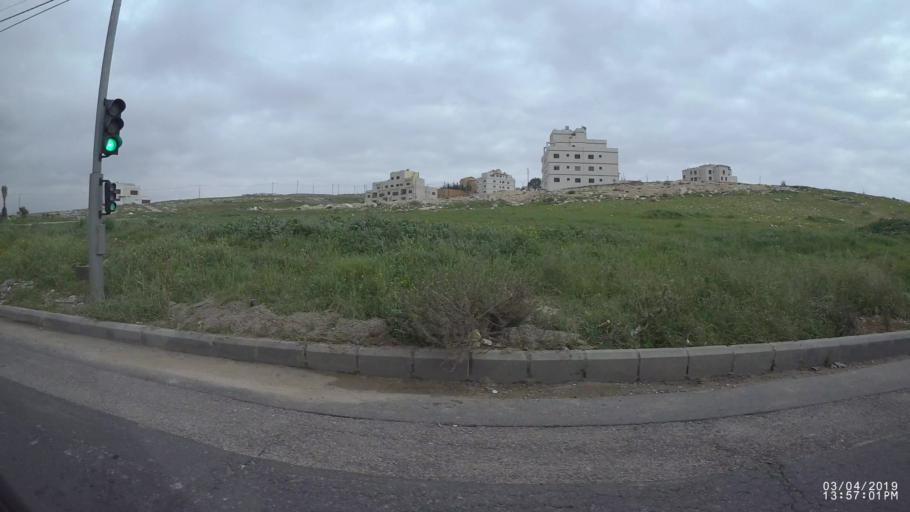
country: JO
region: Amman
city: Wadi as Sir
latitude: 31.9345
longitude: 35.8477
